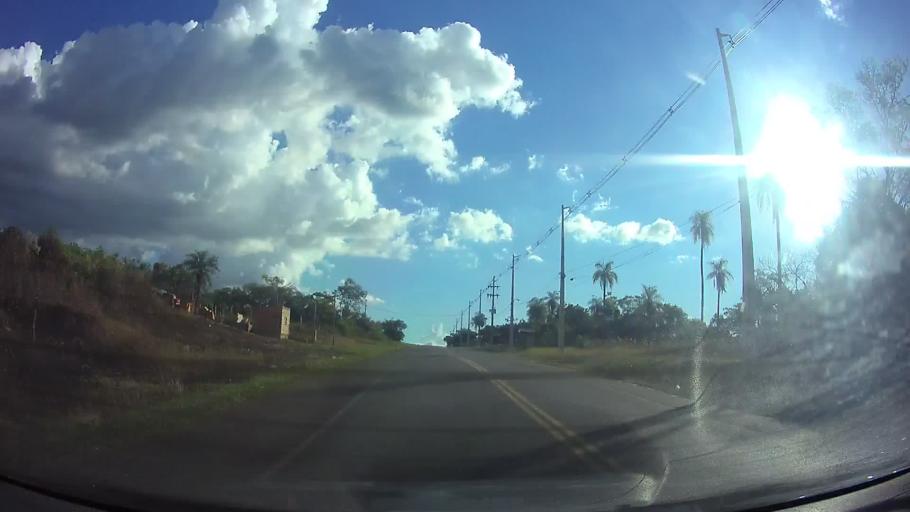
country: PY
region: Cordillera
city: Altos
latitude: -25.2539
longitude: -57.2420
